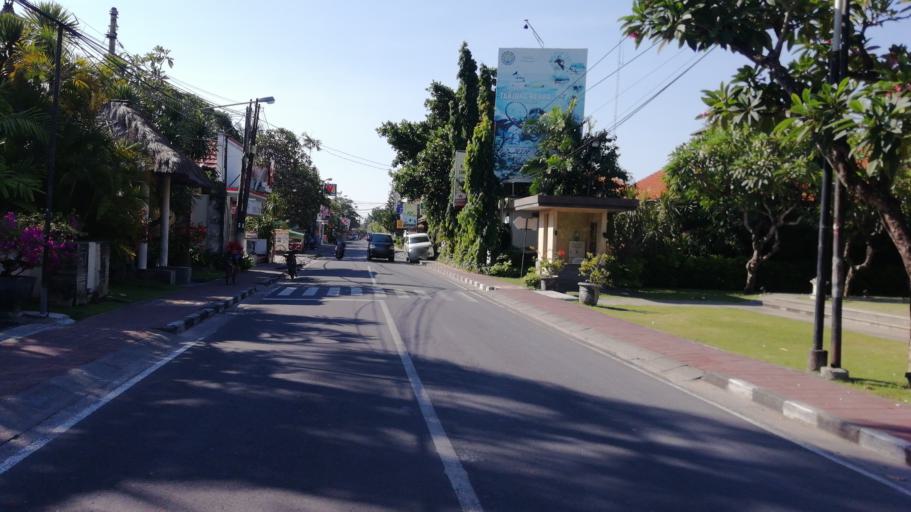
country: ID
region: Bali
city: Bualu
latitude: -8.7587
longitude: 115.2216
